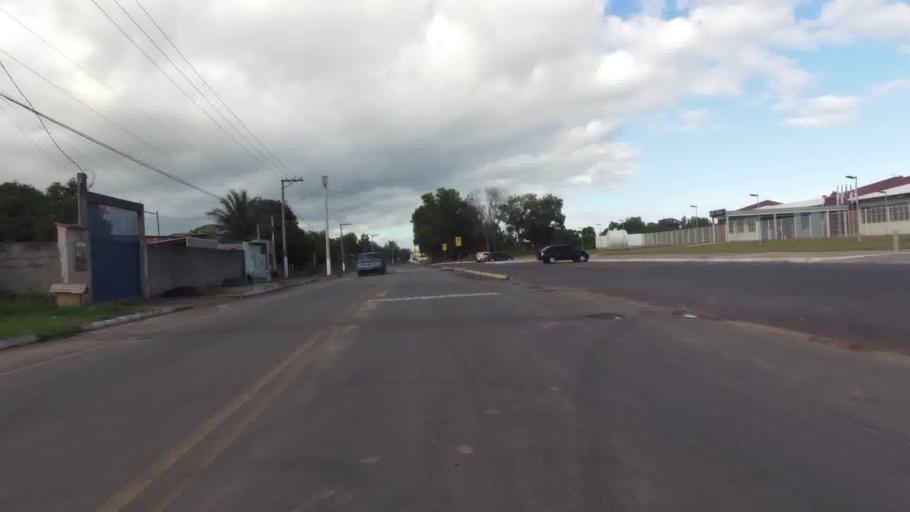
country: BR
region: Espirito Santo
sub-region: Piuma
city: Piuma
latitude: -20.8051
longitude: -40.6351
